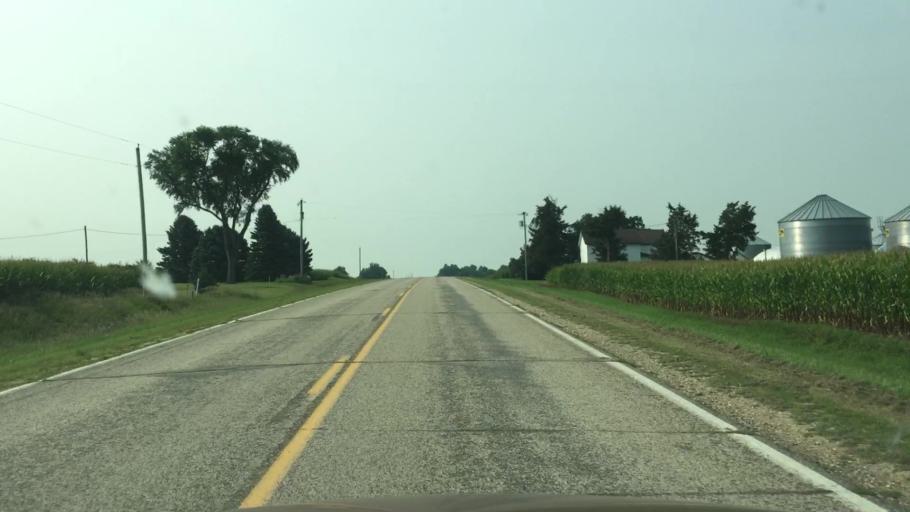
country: US
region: Iowa
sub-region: O'Brien County
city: Sheldon
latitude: 43.2708
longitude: -95.7829
